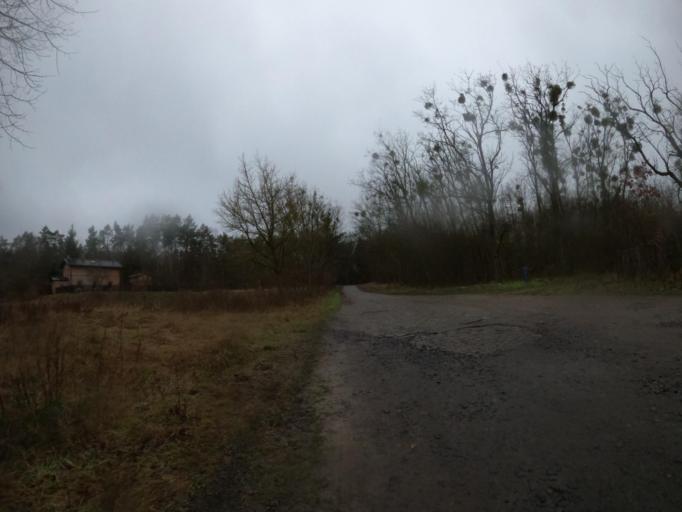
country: PL
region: West Pomeranian Voivodeship
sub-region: Powiat mysliborski
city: Debno
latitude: 52.8021
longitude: 14.7495
